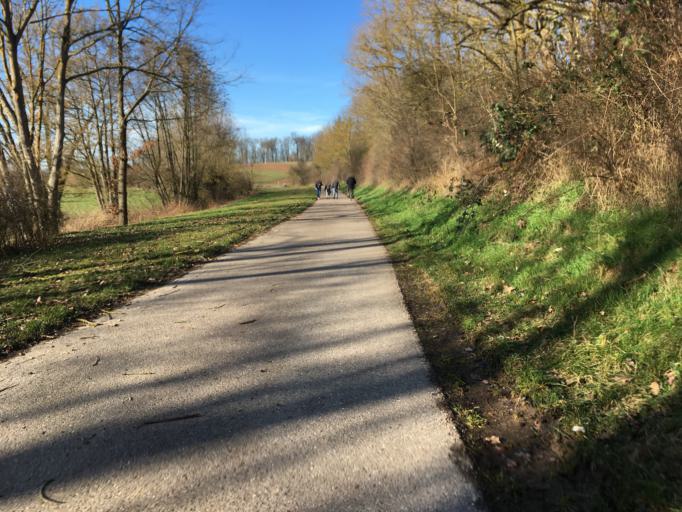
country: DE
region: Baden-Wuerttemberg
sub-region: Regierungsbezirk Stuttgart
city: Eppingen
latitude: 49.1527
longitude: 8.8939
